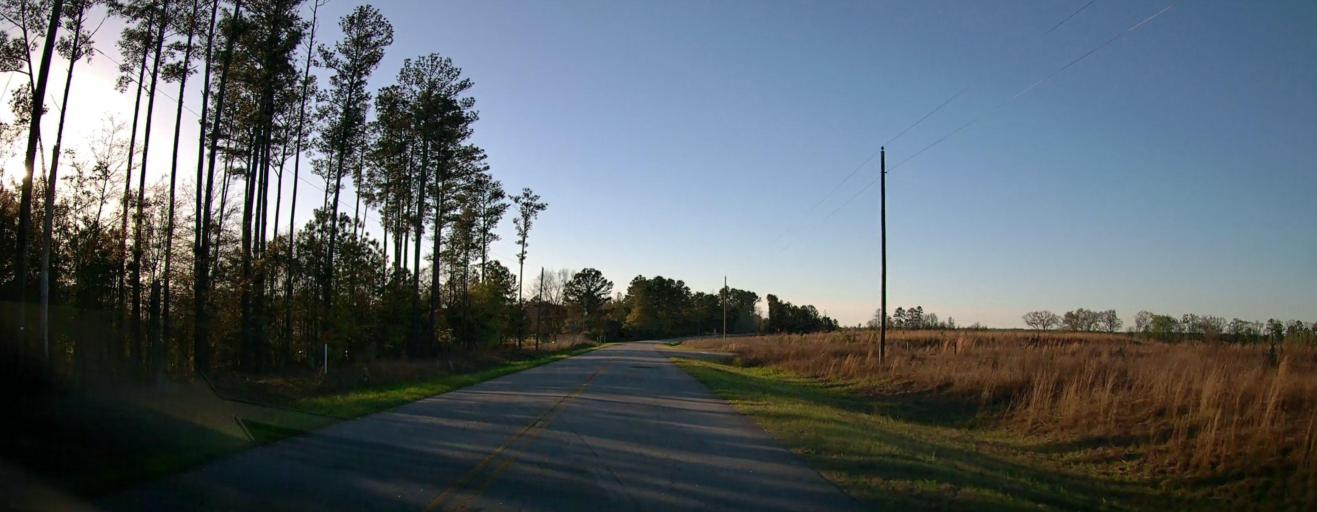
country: US
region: Georgia
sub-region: Wilkinson County
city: Gordon
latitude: 32.8895
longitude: -83.2986
